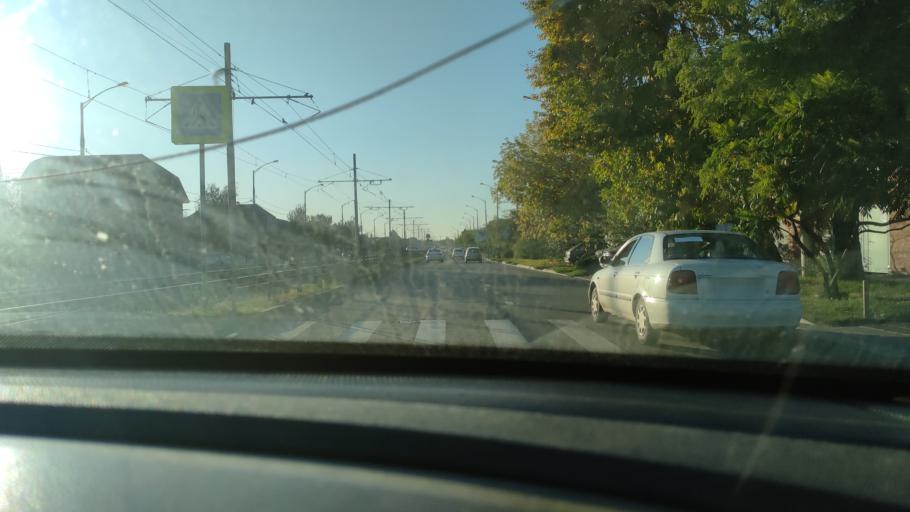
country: RU
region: Krasnodarskiy
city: Krasnodar
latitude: 45.0411
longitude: 38.9479
